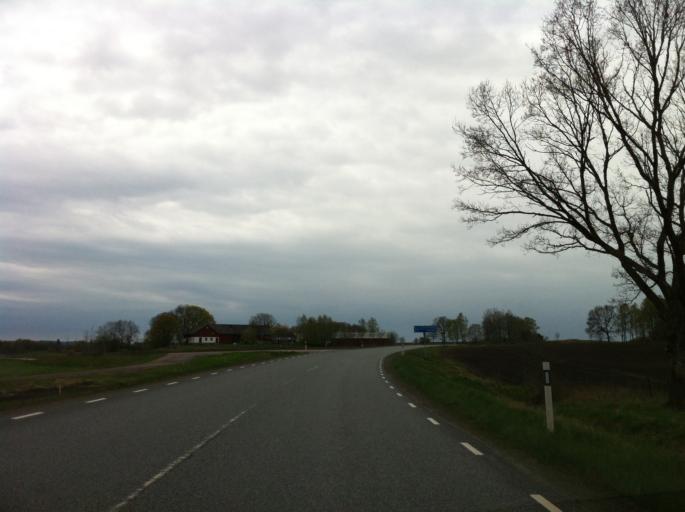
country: SE
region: Halland
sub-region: Falkenbergs Kommun
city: Falkenberg
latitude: 57.0899
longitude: 12.6734
